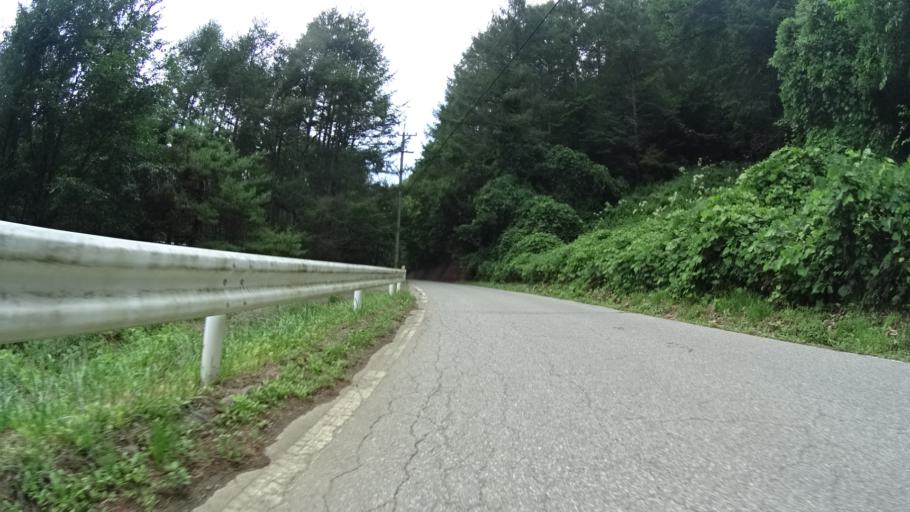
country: JP
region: Nagano
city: Saku
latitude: 36.0700
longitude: 138.6212
